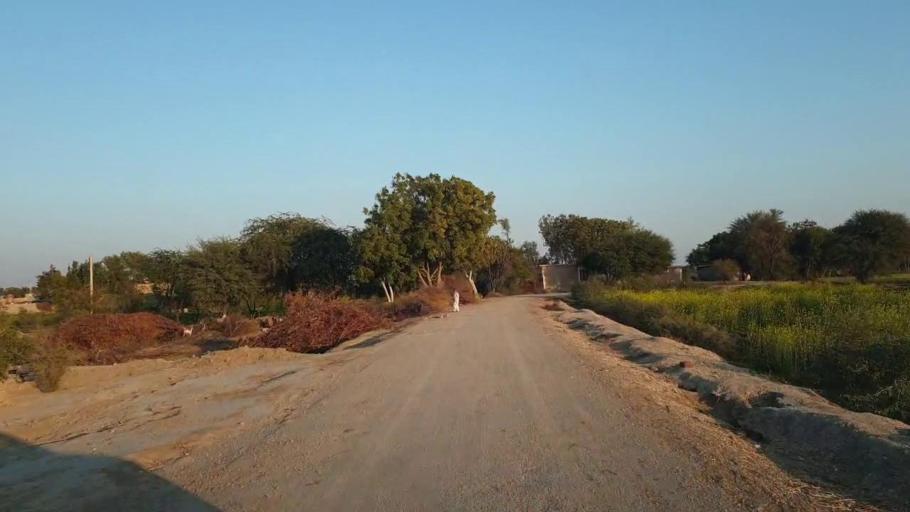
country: PK
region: Sindh
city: Shahpur Chakar
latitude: 26.1511
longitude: 68.5665
